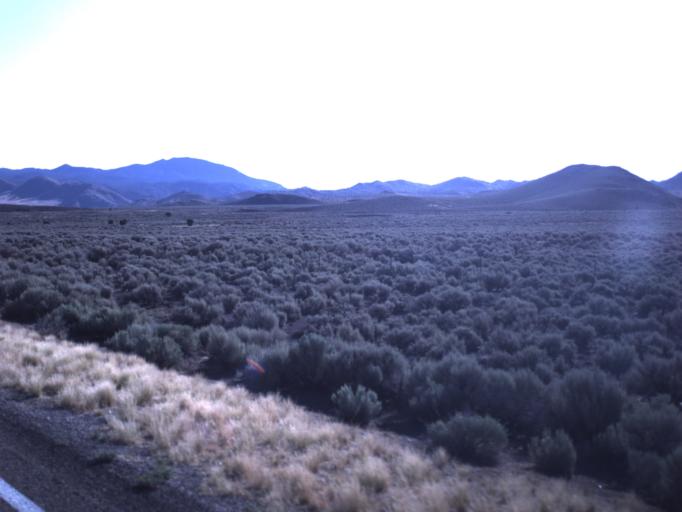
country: US
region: Utah
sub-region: Beaver County
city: Milford
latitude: 38.1899
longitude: -112.9378
